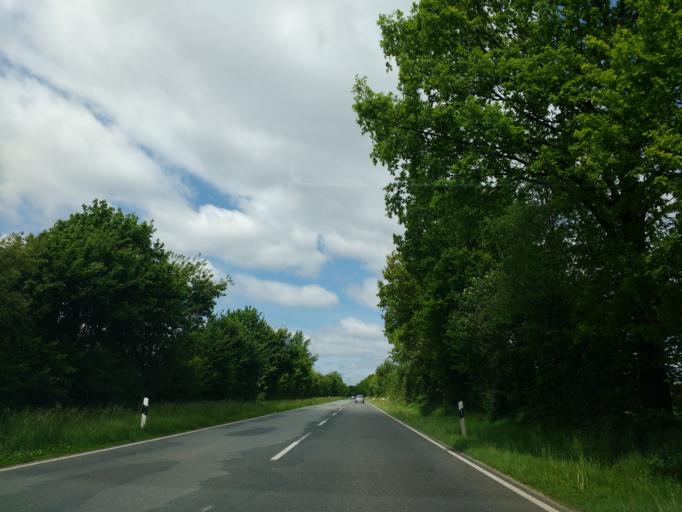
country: DE
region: Schleswig-Holstein
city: Stapelfeld
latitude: 53.5775
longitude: 10.2448
